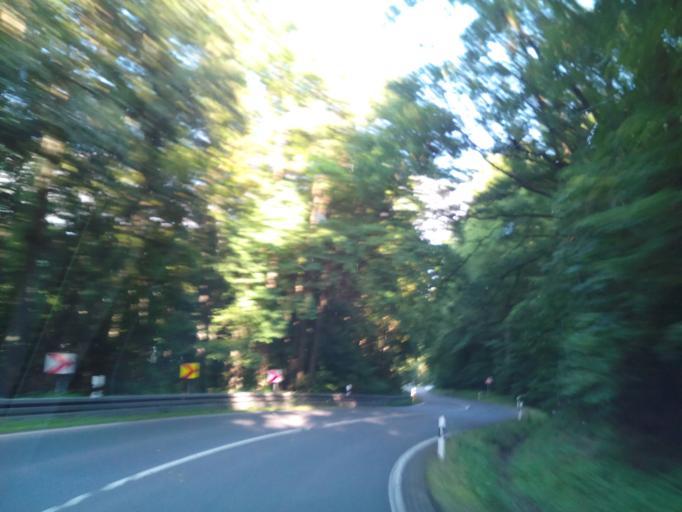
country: DE
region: Bavaria
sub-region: Regierungsbezirk Unterfranken
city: Nudlingen
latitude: 50.2165
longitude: 10.1080
